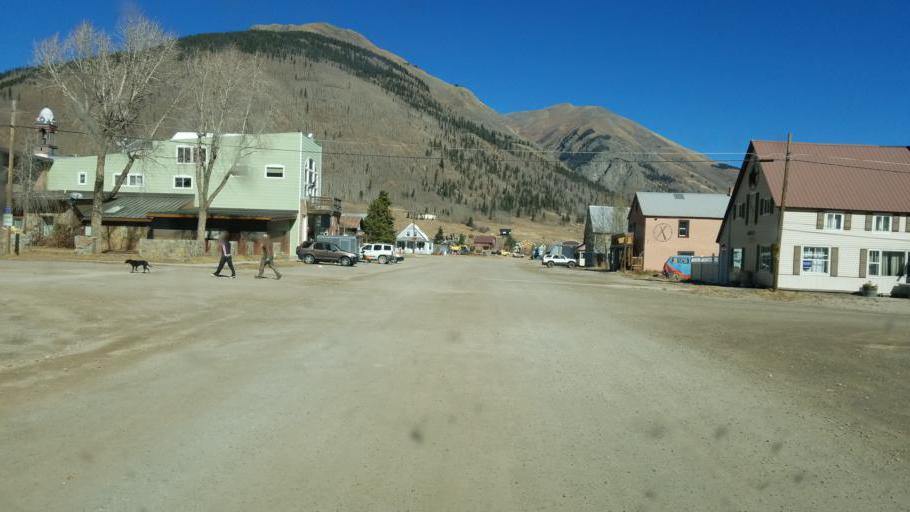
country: US
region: Colorado
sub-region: San Juan County
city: Silverton
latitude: 37.8118
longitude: -107.6629
